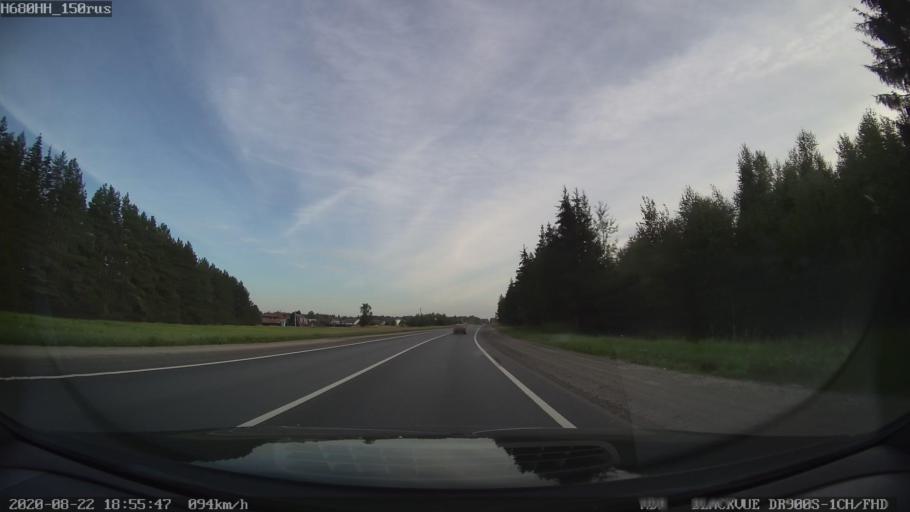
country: RU
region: Tverskaya
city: Rameshki
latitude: 57.1932
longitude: 36.0843
